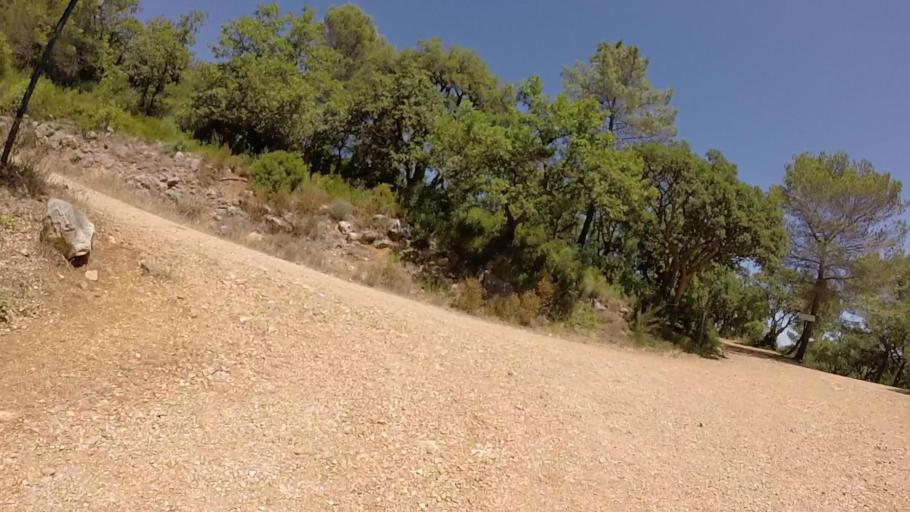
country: FR
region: Provence-Alpes-Cote d'Azur
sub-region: Departement des Alpes-Maritimes
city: Valbonne
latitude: 43.6319
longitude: 7.0335
